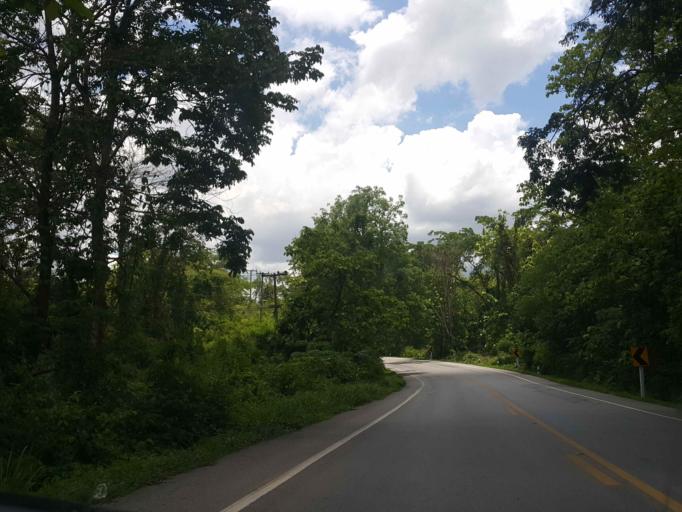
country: TH
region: Nan
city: Wiang Sa
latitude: 18.5228
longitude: 100.5755
